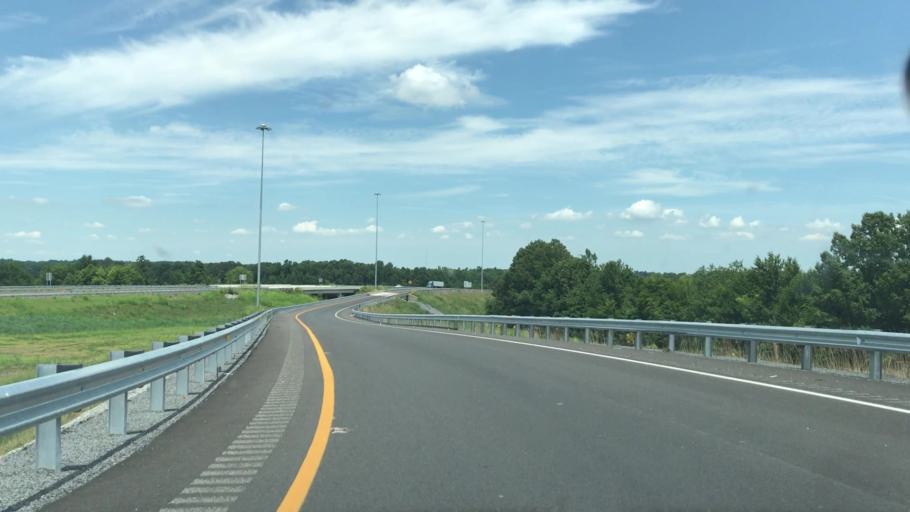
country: US
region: Kentucky
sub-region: Marshall County
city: Benton
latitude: 36.8686
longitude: -88.3632
